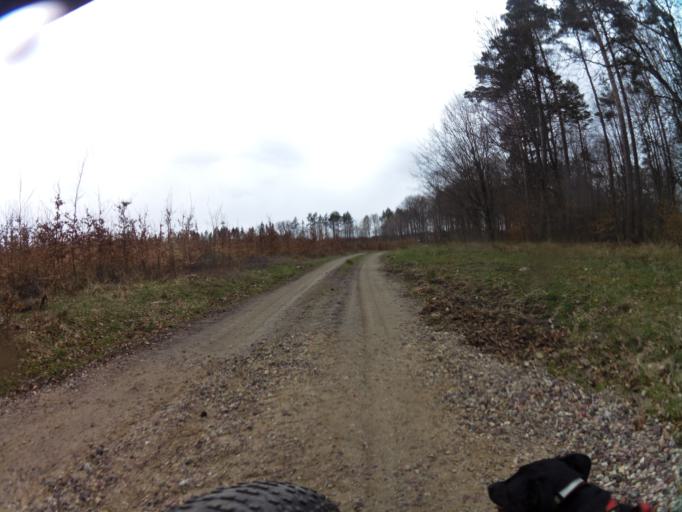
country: PL
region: West Pomeranian Voivodeship
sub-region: Powiat koszalinski
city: Polanow
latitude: 54.0740
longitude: 16.6203
